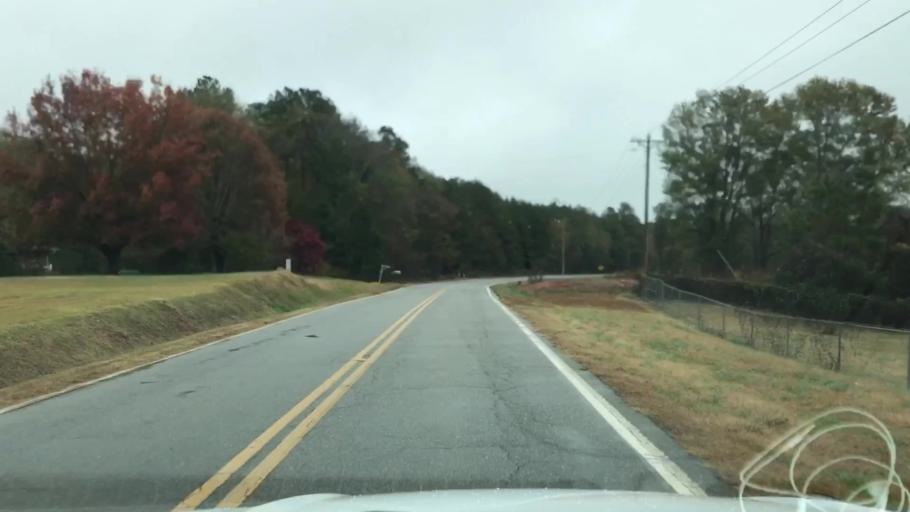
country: US
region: South Carolina
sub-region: Spartanburg County
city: Woodruff
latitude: 34.7473
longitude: -81.9452
